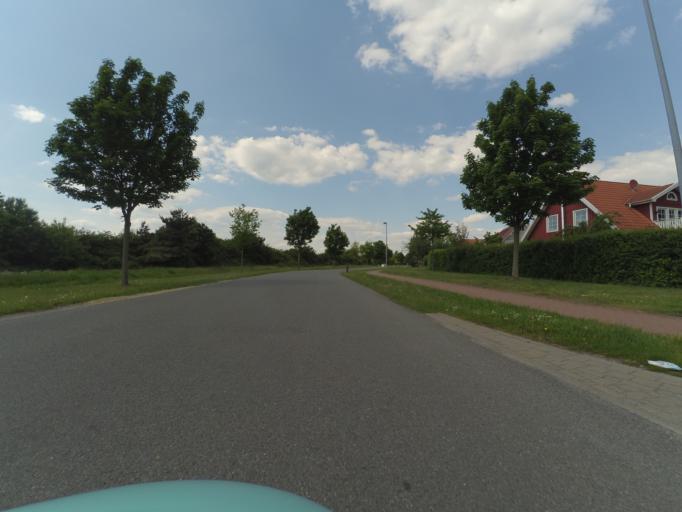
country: DE
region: Lower Saxony
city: Haenigsen
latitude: 52.4783
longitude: 10.0868
